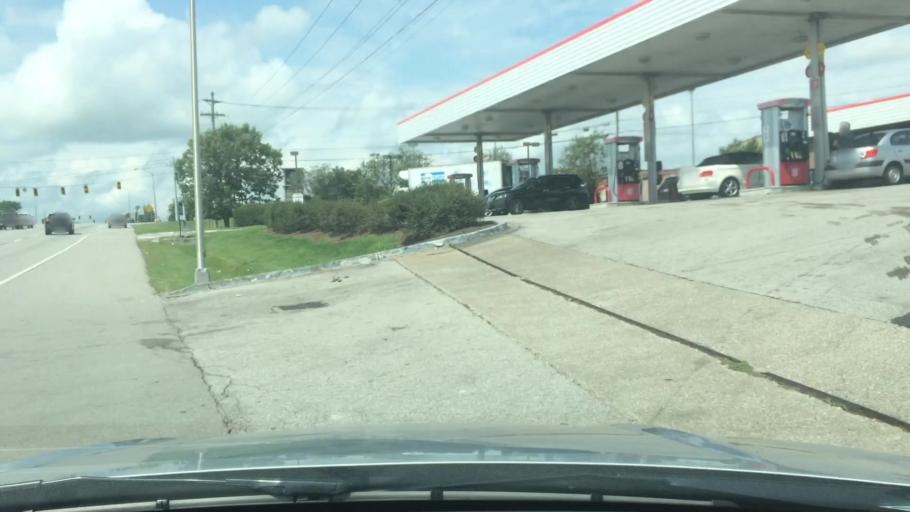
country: US
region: Kentucky
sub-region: Franklin County
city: Frankfort
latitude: 38.1630
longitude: -84.8955
